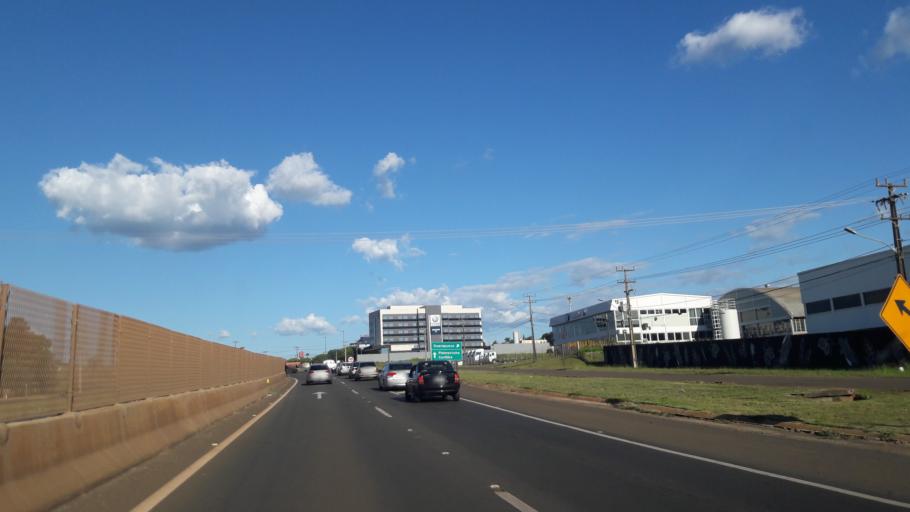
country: BR
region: Parana
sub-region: Guarapuava
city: Guarapuava
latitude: -25.3657
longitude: -51.4801
